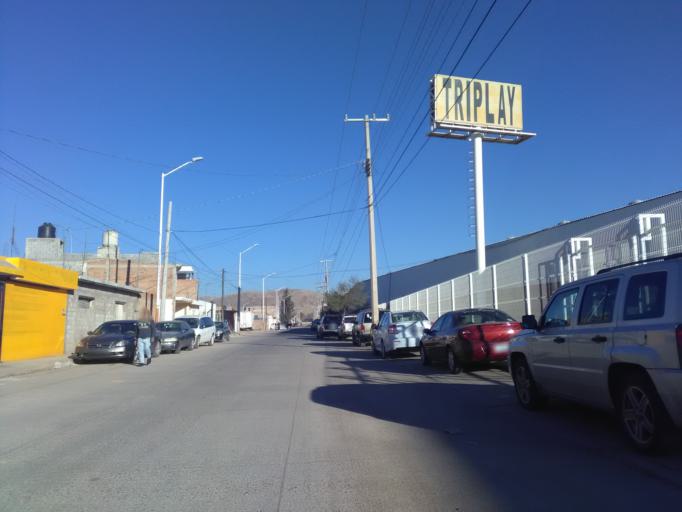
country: MX
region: Durango
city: Victoria de Durango
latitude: 24.0525
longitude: -104.6522
